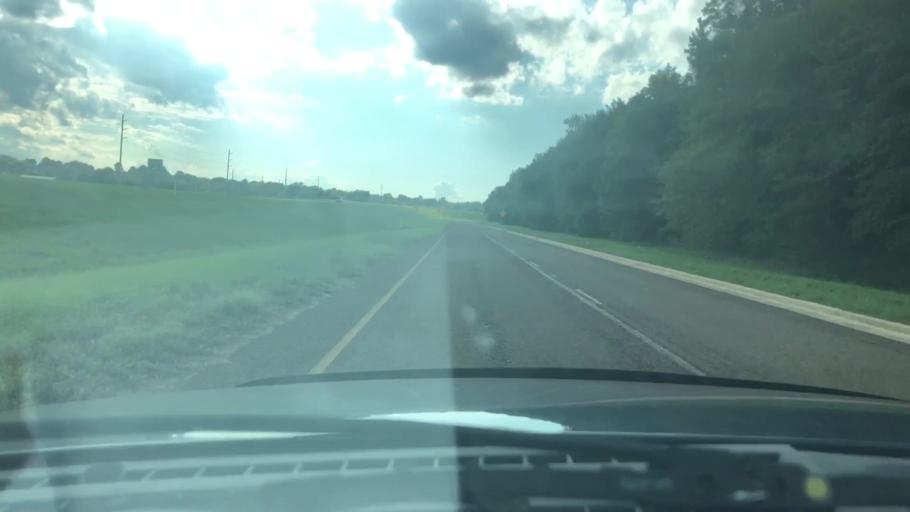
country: US
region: Texas
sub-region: Bowie County
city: Wake Village
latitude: 33.3864
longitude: -94.0834
